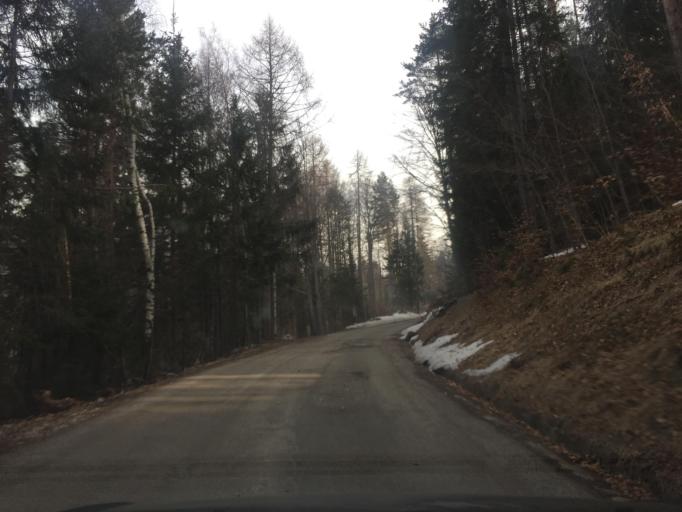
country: IT
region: Friuli Venezia Giulia
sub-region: Provincia di Udine
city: Tarvisio
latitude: 46.5053
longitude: 13.6381
